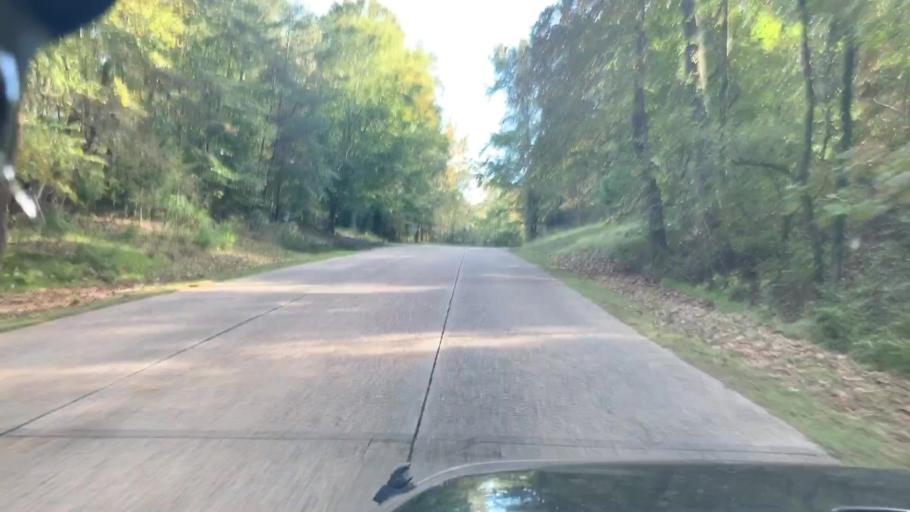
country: US
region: Virginia
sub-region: City of Williamsburg
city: Williamsburg
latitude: 37.2618
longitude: -76.7022
